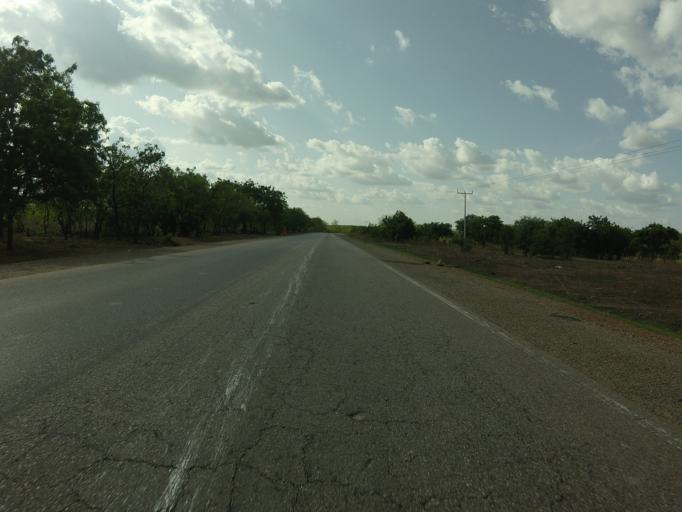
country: GH
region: Upper East
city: Bolgatanga
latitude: 10.5615
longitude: -0.8334
